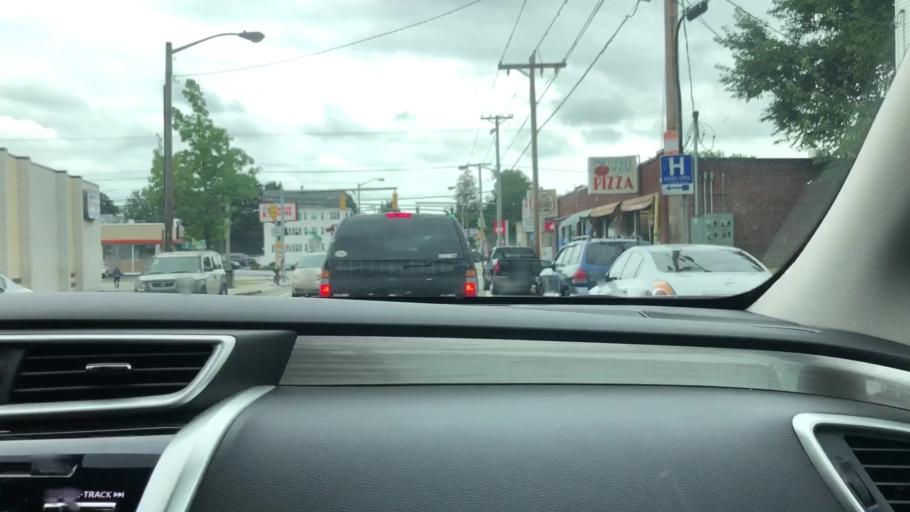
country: US
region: Rhode Island
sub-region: Providence County
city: Central Falls
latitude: 41.8718
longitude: -71.4140
